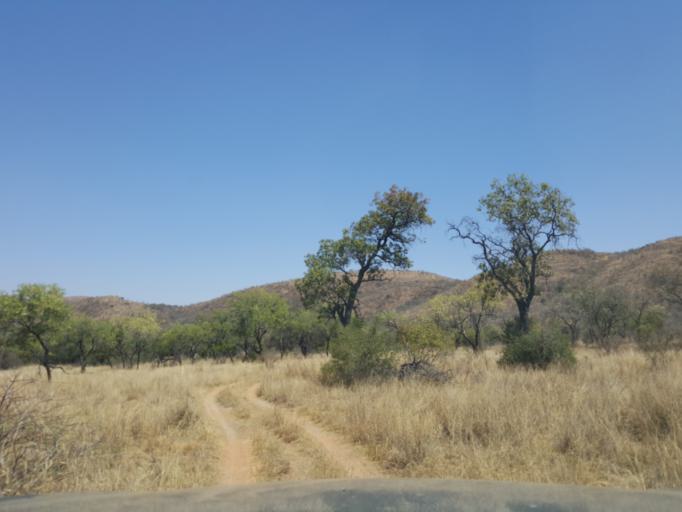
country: BW
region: South East
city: Lobatse
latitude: -25.1414
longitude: 25.6706
